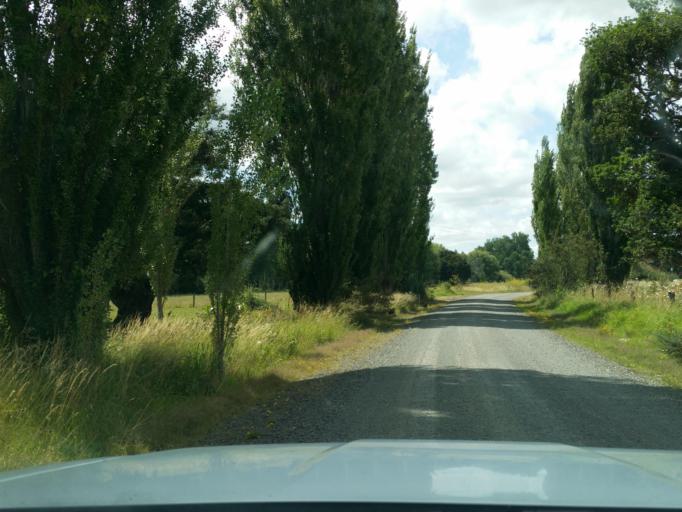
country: NZ
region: Northland
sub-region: Kaipara District
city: Dargaville
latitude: -35.7913
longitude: 173.7306
